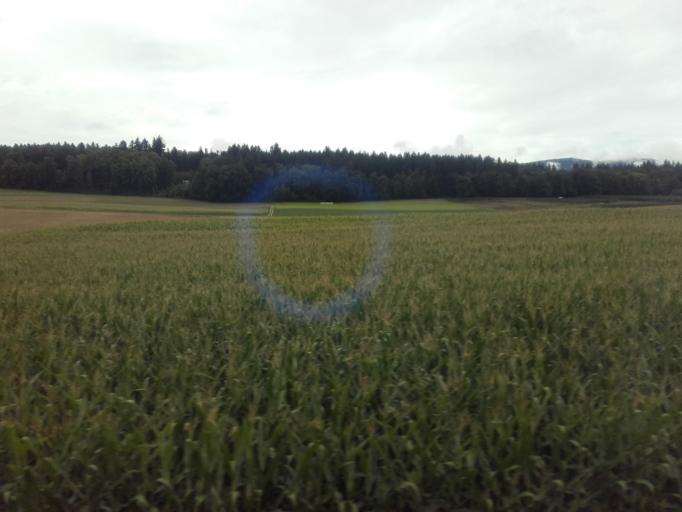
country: CH
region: Solothurn
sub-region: Bezirk Wasseramt
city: Biberist
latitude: 47.1748
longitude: 7.5427
